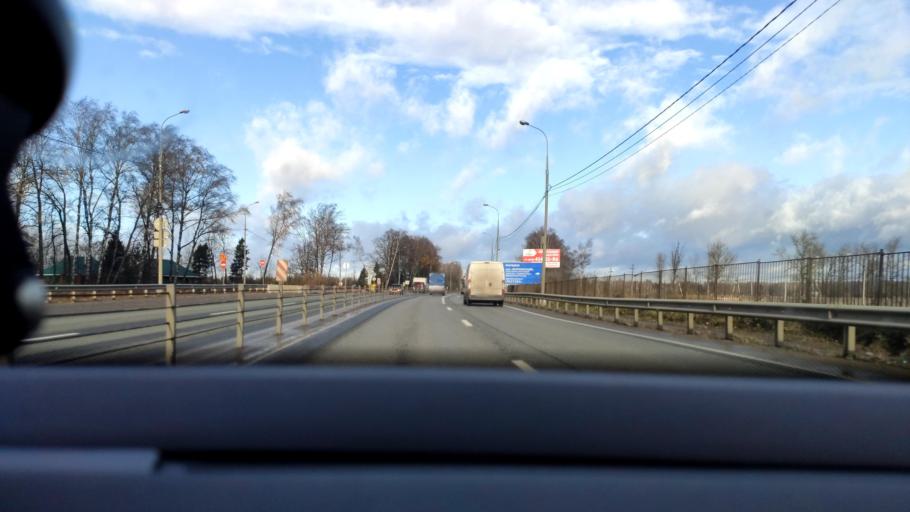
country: RU
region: Moskovskaya
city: Nekrasovskiy
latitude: 56.0863
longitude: 37.5239
